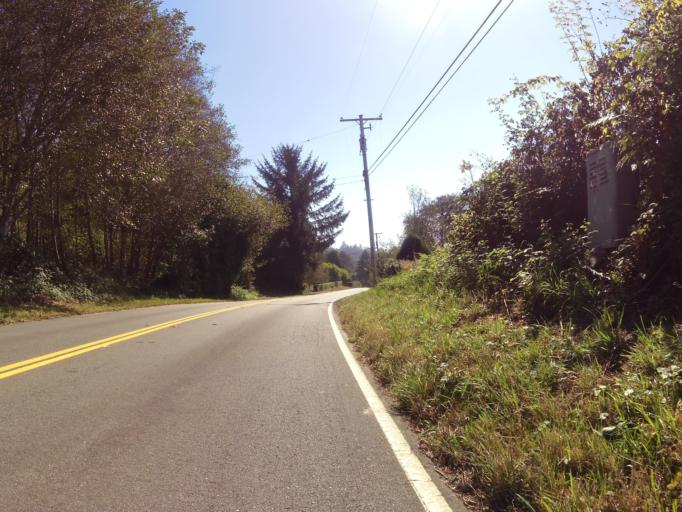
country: US
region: Oregon
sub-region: Curry County
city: Harbor
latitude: 41.9662
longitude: -124.1984
